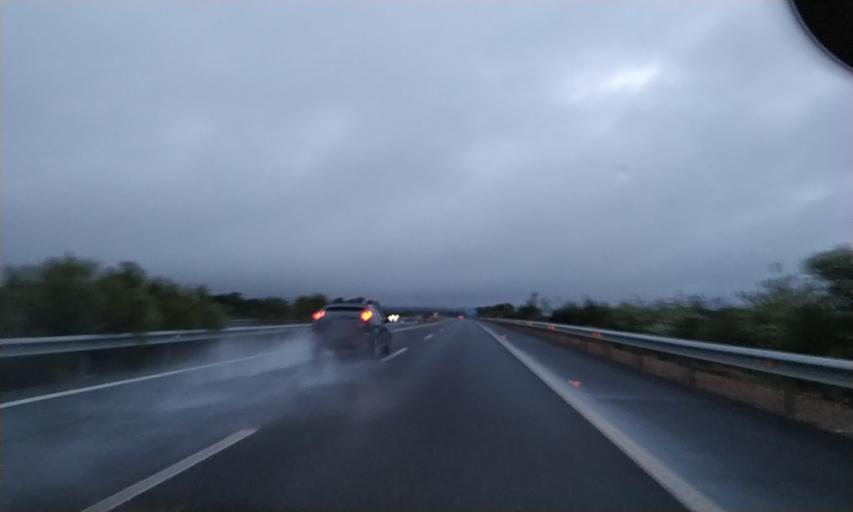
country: ES
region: Extremadura
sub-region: Provincia de Badajoz
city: Aljucen
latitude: 39.0990
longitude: -6.2860
